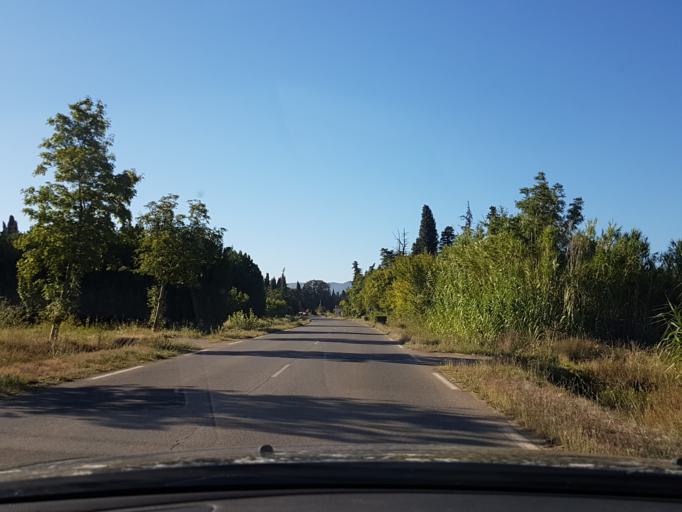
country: FR
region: Provence-Alpes-Cote d'Azur
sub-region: Departement des Bouches-du-Rhone
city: Eygalieres
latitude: 43.7792
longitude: 4.9580
